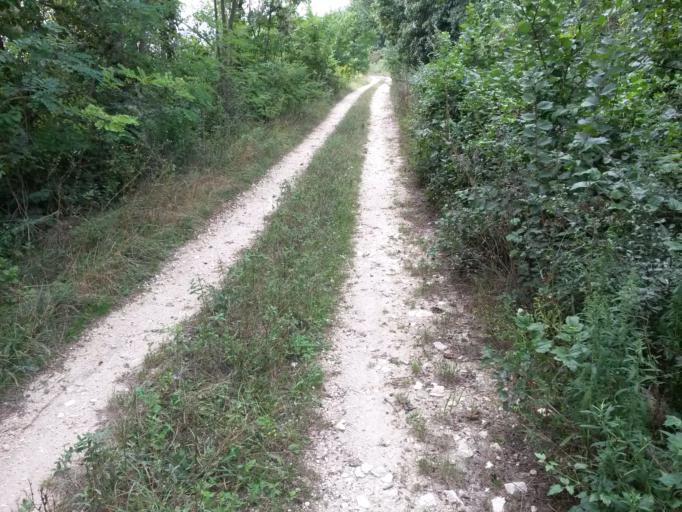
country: HU
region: Pest
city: Perbal
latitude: 47.5950
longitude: 18.8012
